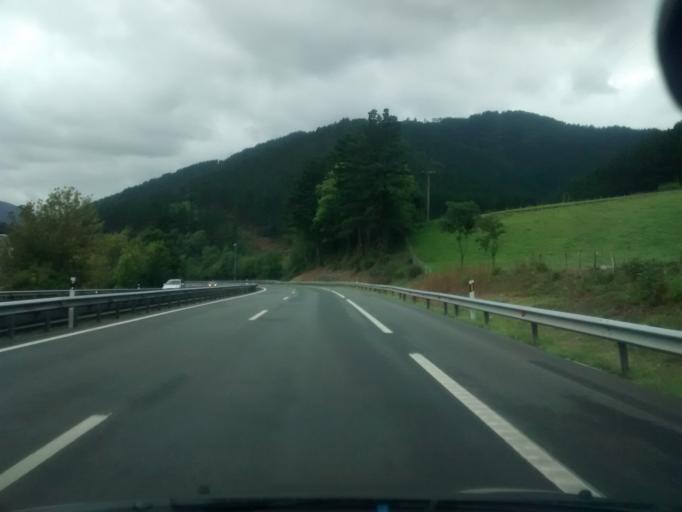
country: ES
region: Basque Country
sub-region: Provincia de Guipuzcoa
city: Mendaro
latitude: 43.2512
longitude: -2.3916
